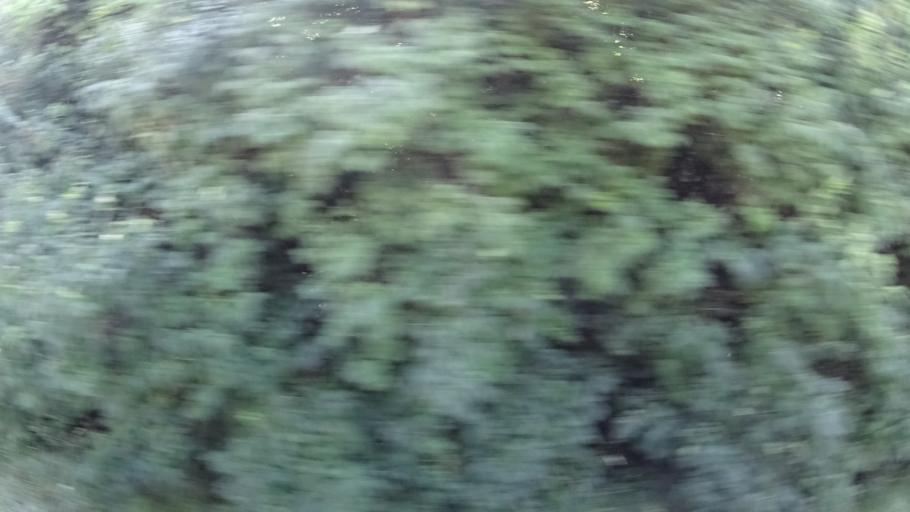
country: US
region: Ohio
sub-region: Erie County
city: Sandusky
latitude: 41.4064
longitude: -82.7458
